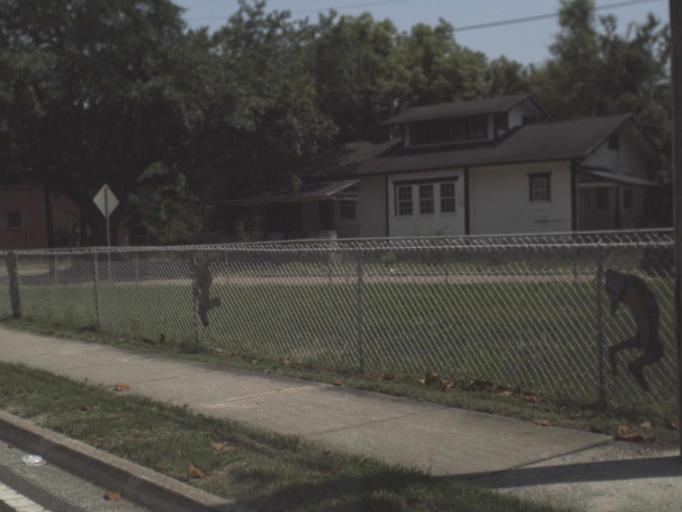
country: US
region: Florida
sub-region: Duval County
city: Jacksonville
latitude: 30.3622
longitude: -81.6607
